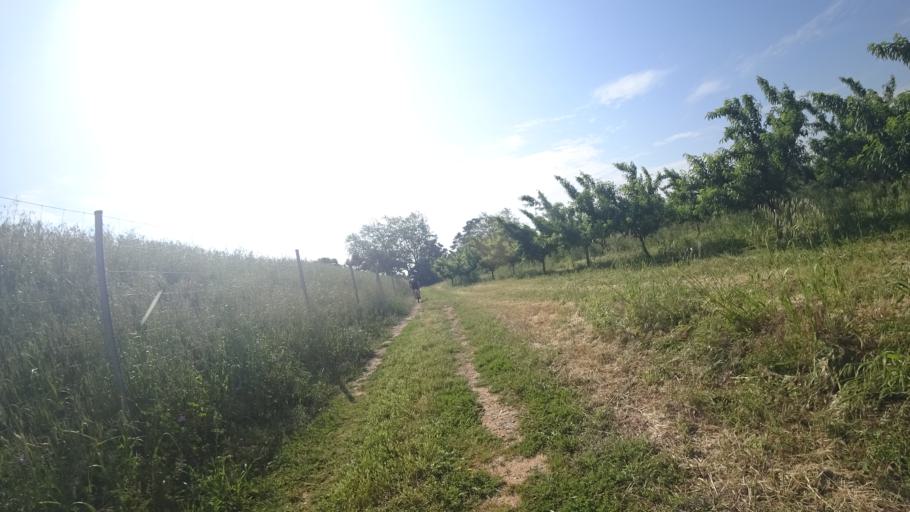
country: FR
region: Languedoc-Roussillon
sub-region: Departement de l'Aude
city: Saint-Marcel-sur-Aude
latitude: 43.2771
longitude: 2.9141
